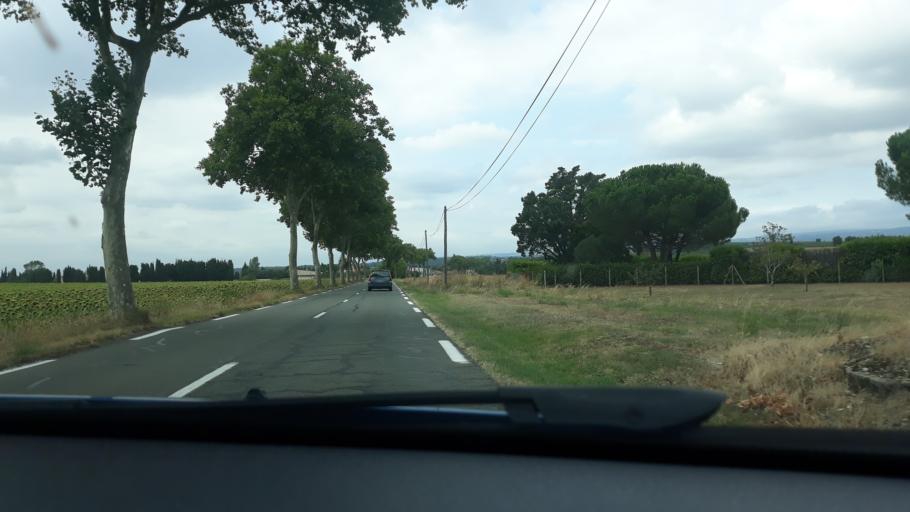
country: FR
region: Languedoc-Roussillon
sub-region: Departement de l'Aude
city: Pezens
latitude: 43.2617
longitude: 2.2459
